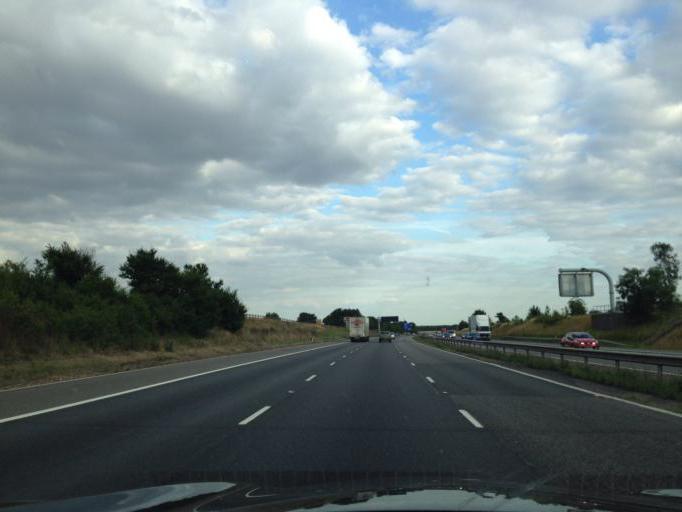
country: GB
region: England
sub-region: Oxfordshire
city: Somerton
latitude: 51.9638
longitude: -1.2273
